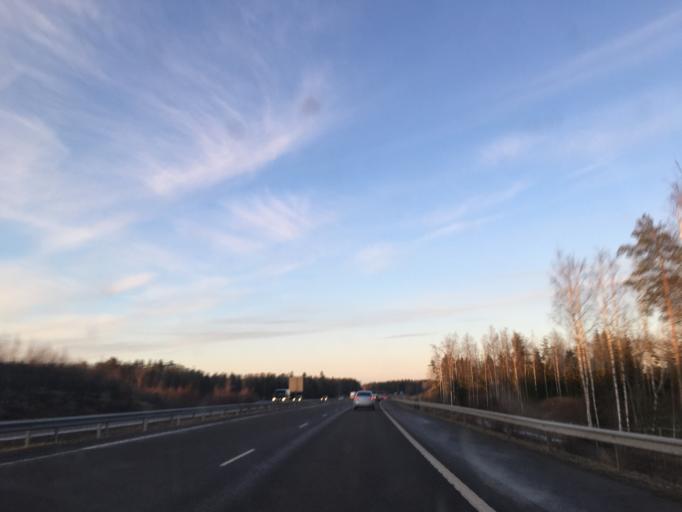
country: FI
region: Varsinais-Suomi
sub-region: Turku
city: Turku
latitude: 60.5162
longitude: 22.3029
